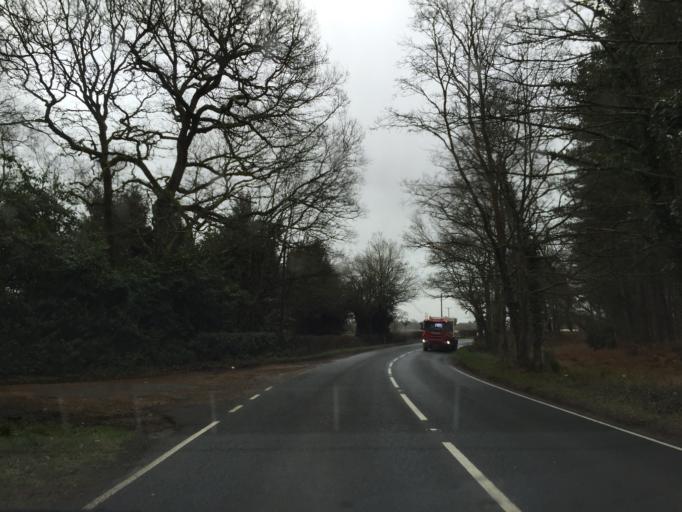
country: GB
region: England
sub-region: Hampshire
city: Ringwood
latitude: 50.8490
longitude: -1.8122
